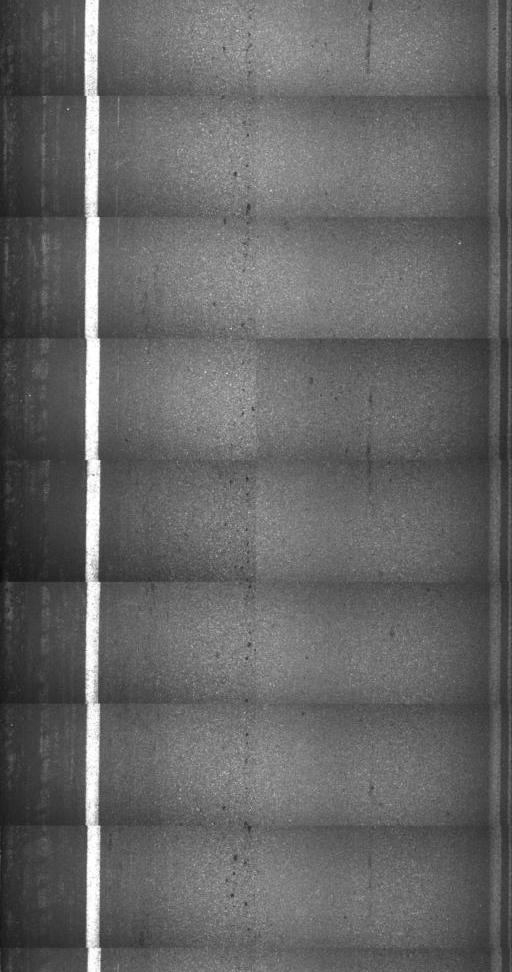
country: US
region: Vermont
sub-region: Orange County
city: Randolph
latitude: 43.8514
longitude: -72.5825
